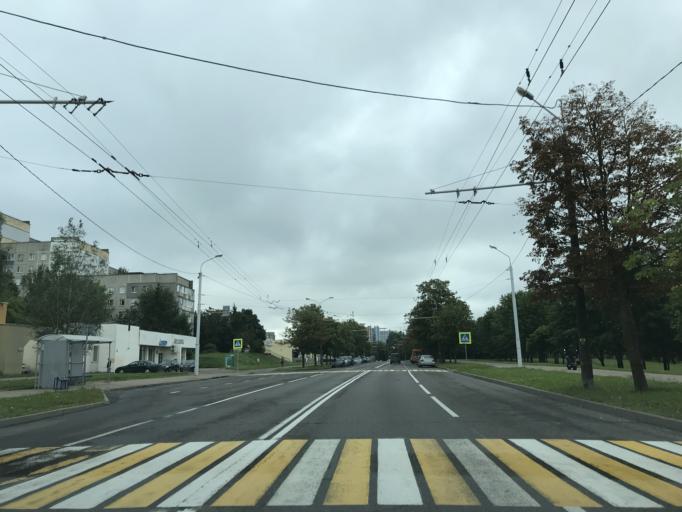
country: BY
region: Minsk
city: Borovlyany
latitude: 53.9529
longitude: 27.6318
